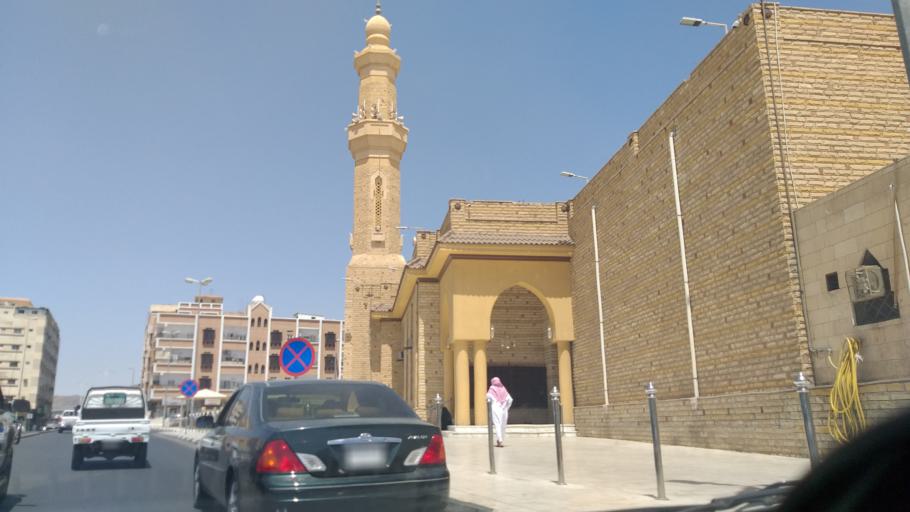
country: SA
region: Makkah
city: Ta'if
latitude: 21.2698
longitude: 40.4086
